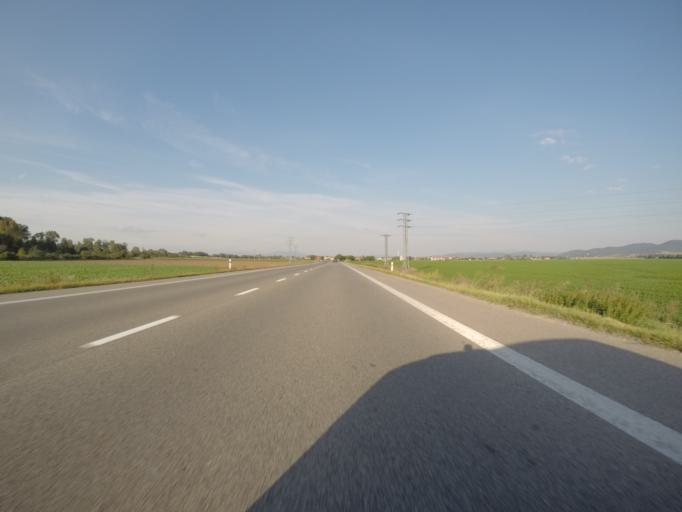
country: SK
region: Nitriansky
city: Banovce nad Bebravou
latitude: 48.5606
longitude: 18.1983
